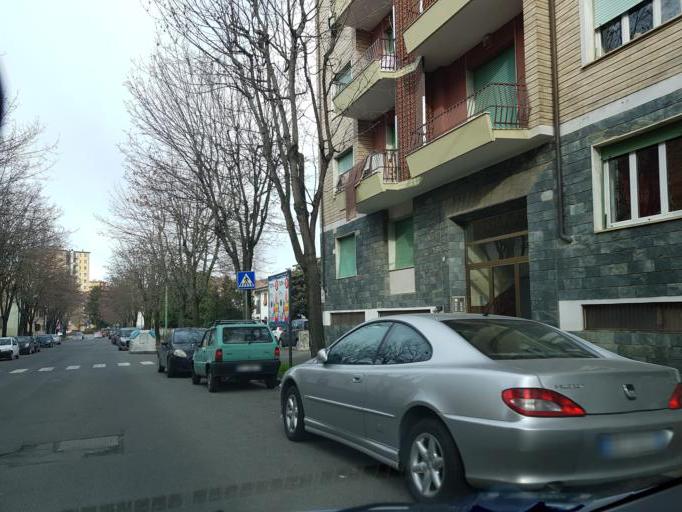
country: IT
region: Piedmont
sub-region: Provincia di Alessandria
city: Novi Ligure
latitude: 44.7615
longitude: 8.7968
